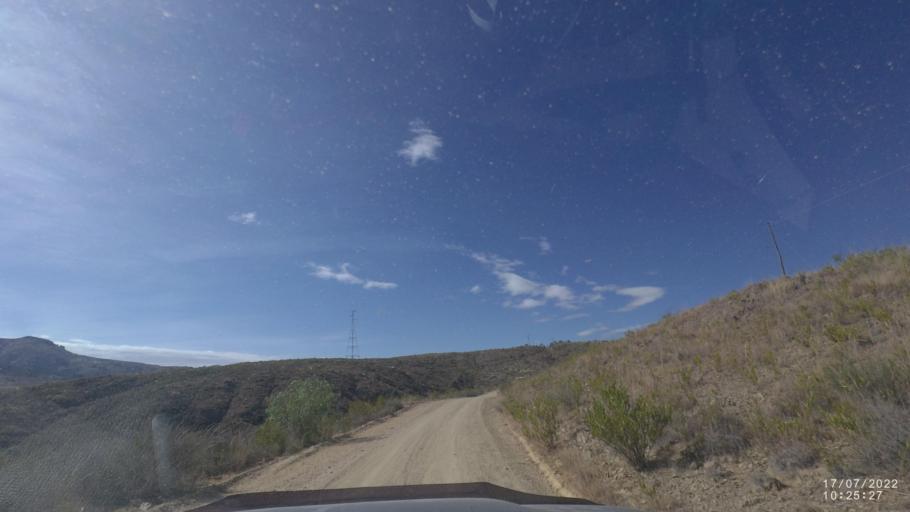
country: BO
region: Cochabamba
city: Capinota
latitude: -17.6173
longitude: -66.1717
